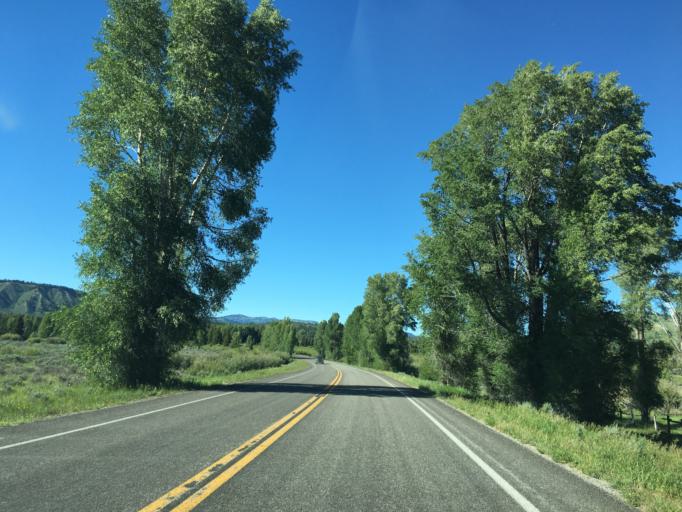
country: US
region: Wyoming
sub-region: Teton County
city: Jackson
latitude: 43.8285
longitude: -110.5141
